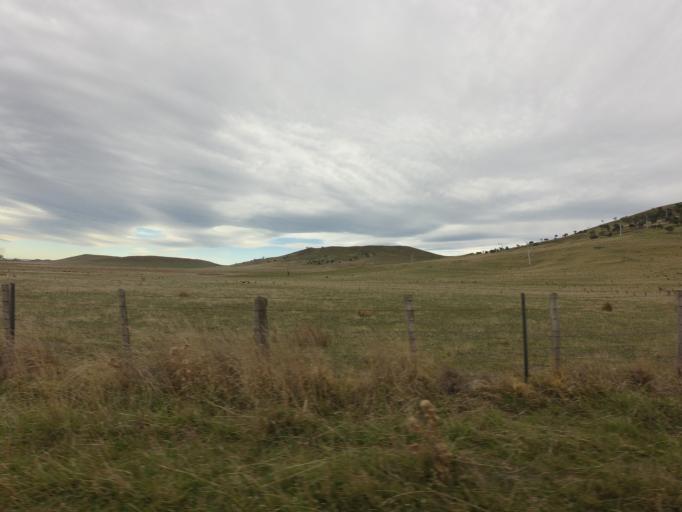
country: AU
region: Tasmania
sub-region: Derwent Valley
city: New Norfolk
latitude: -42.3794
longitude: 146.8668
